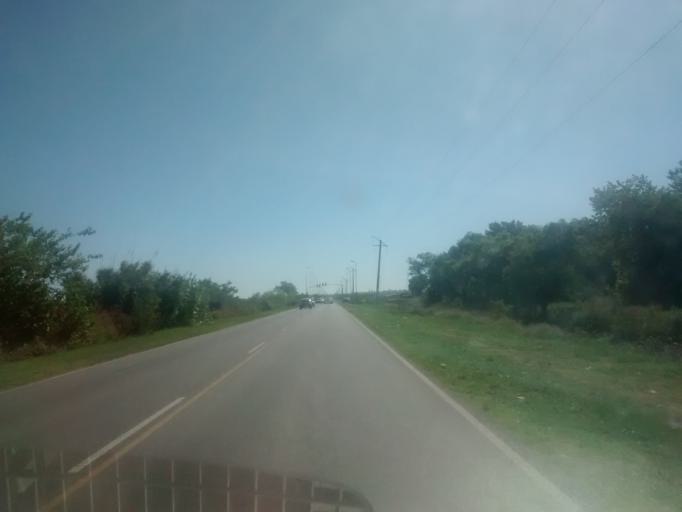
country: AR
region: Buenos Aires
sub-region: Partido de Berisso
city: Berisso
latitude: -34.8903
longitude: -57.8697
